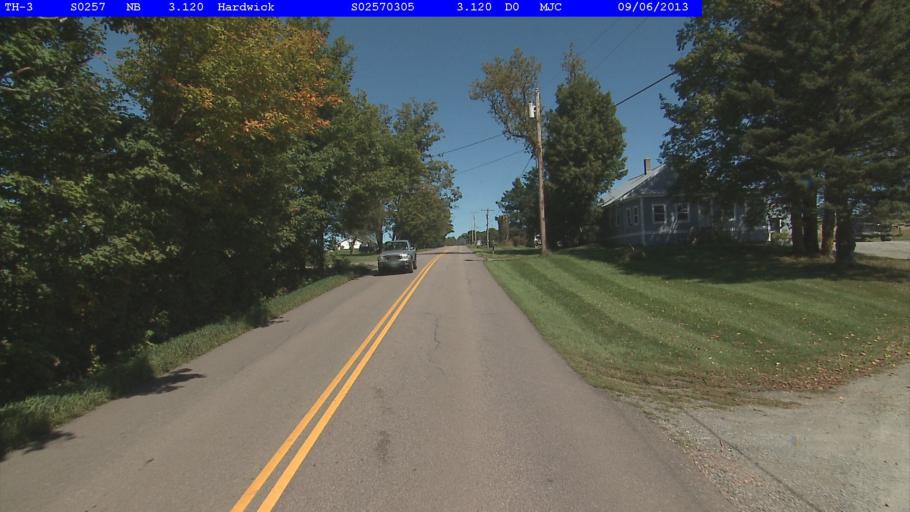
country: US
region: Vermont
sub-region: Caledonia County
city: Hardwick
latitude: 44.5346
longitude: -72.3324
